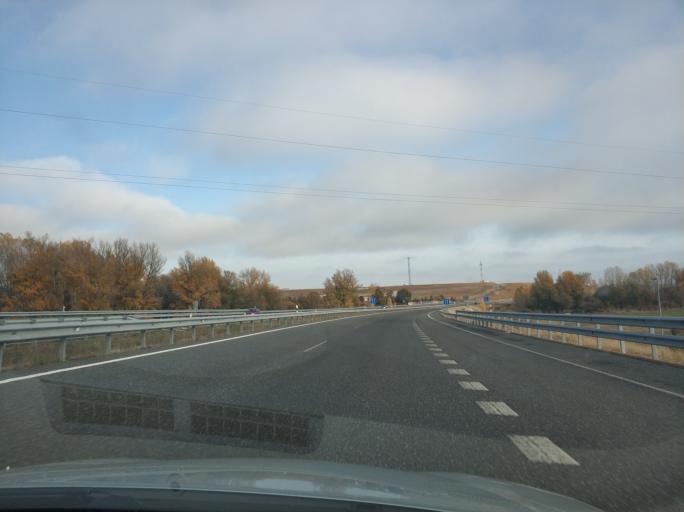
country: ES
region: Castille and Leon
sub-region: Provincia de Leon
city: Valdefresno
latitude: 42.5638
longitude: -5.4836
